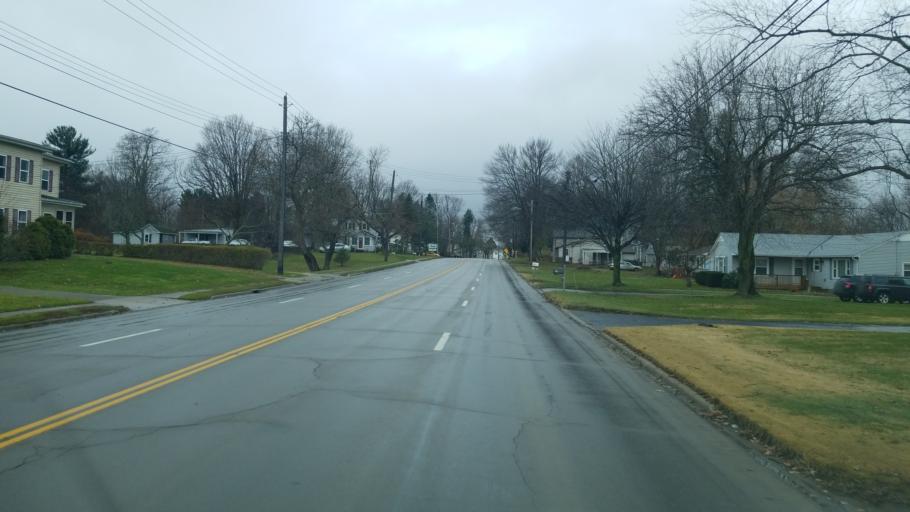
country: US
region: Ohio
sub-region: Ashtabula County
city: North Kingsville
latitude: 41.9086
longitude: -80.6851
